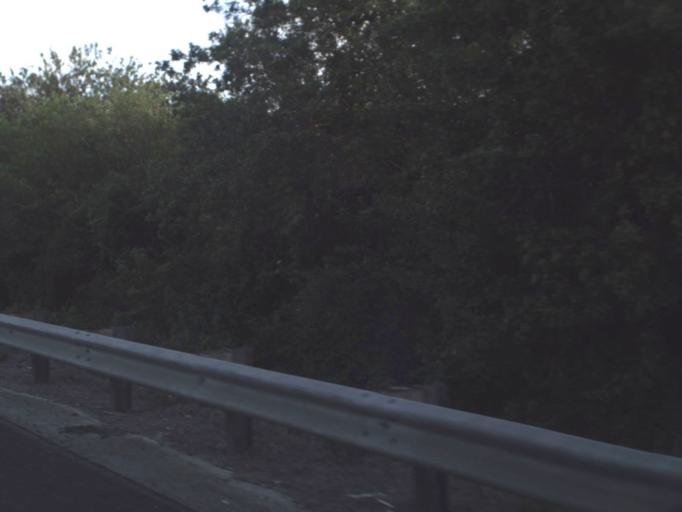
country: US
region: Florida
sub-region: Brevard County
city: Rockledge
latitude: 28.2715
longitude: -80.6919
